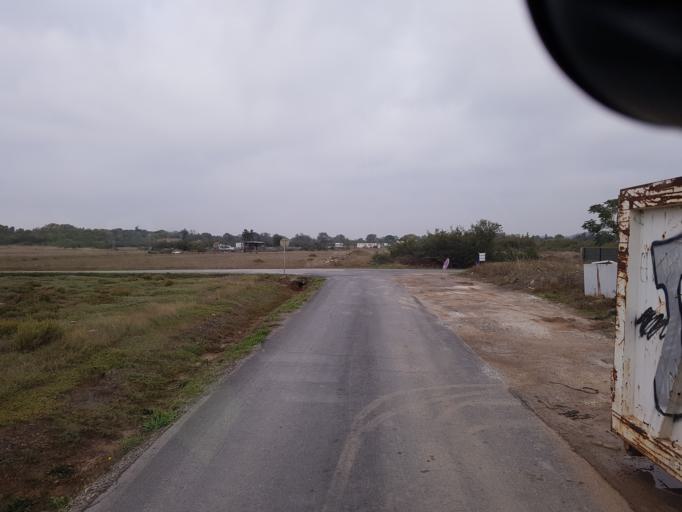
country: FR
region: Languedoc-Roussillon
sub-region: Departement de l'Herault
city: Marseillan
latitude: 43.3652
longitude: 3.5368
